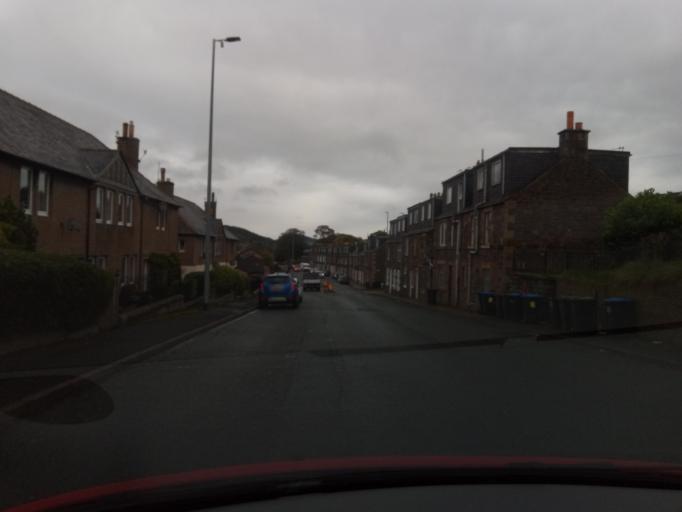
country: GB
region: Scotland
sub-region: The Scottish Borders
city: Galashiels
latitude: 55.6253
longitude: -2.8303
